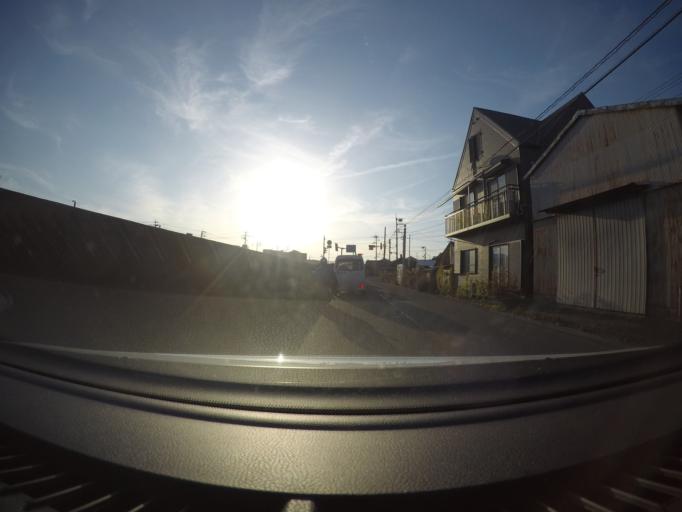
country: JP
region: Kochi
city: Kochi-shi
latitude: 33.5424
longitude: 133.5752
